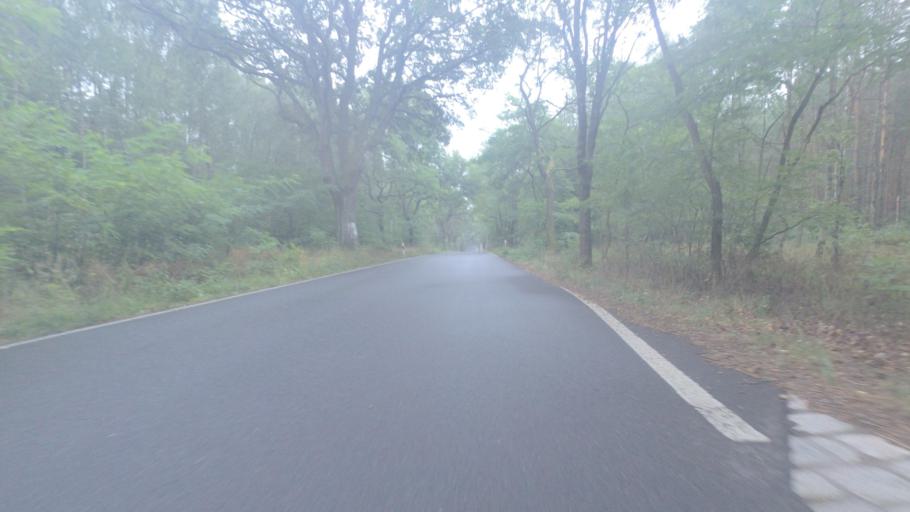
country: DE
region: Brandenburg
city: Heiligengrabe
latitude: 53.1563
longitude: 12.3450
